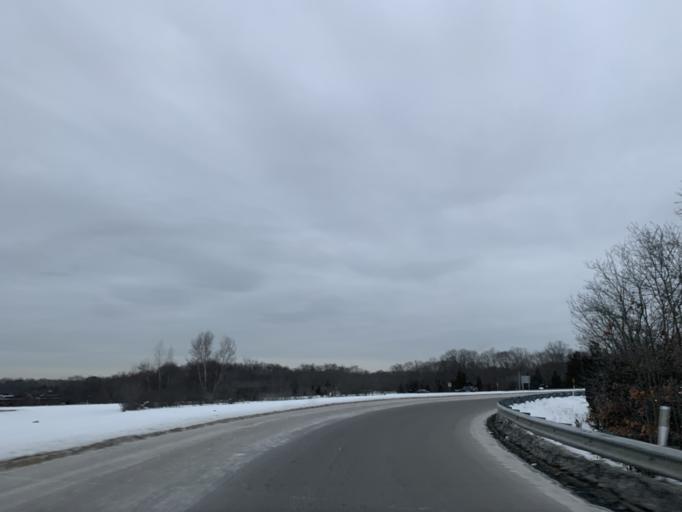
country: US
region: Massachusetts
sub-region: Norfolk County
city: Avon
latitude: 42.0942
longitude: -71.0569
